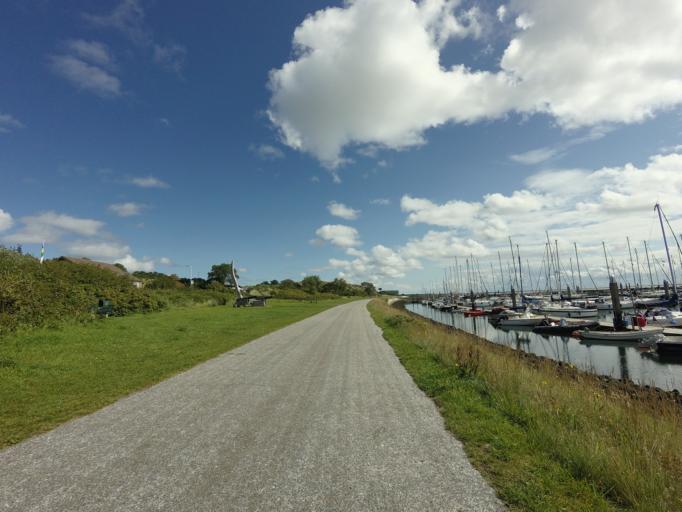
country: NL
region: Friesland
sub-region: Gemeente Terschelling
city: West-Terschelling
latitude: 53.3656
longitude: 5.2229
